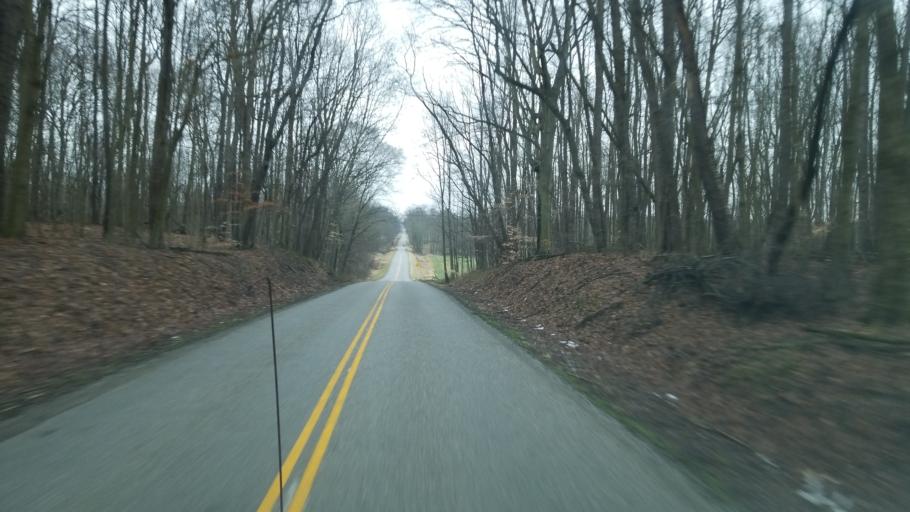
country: US
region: Ohio
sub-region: Wayne County
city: Orrville
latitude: 40.8849
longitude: -81.7835
